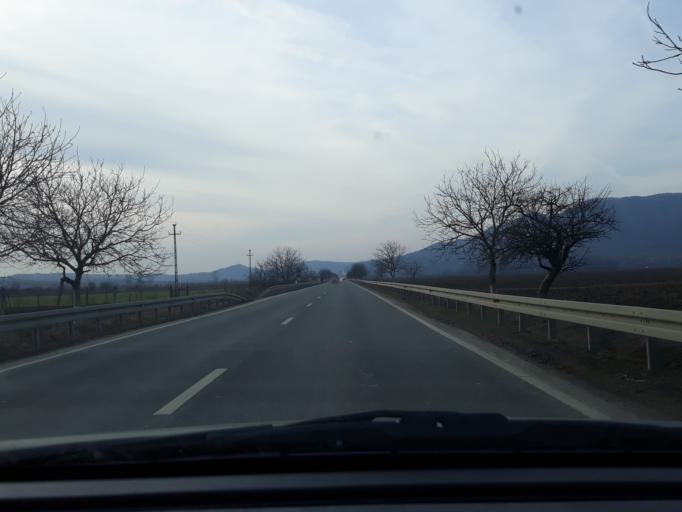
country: RO
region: Salaj
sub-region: Comuna Periceiu
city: Periceiu
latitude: 47.2278
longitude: 22.8517
